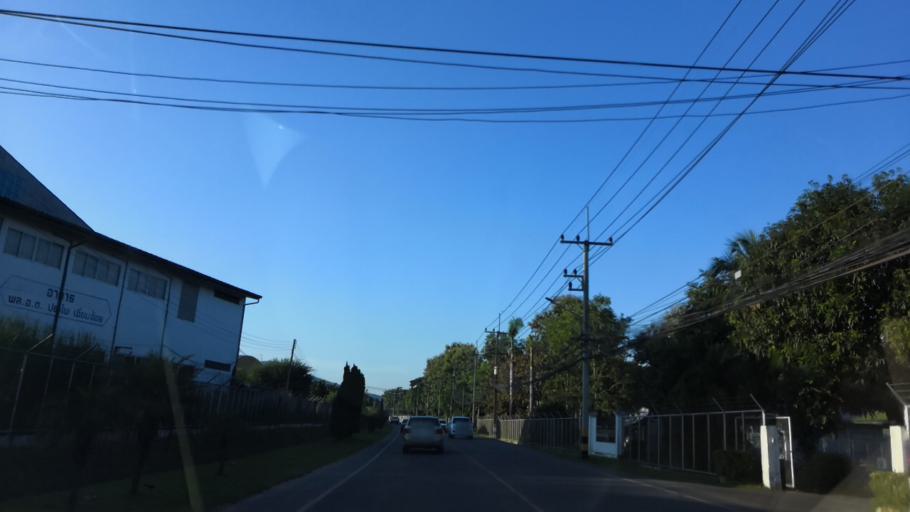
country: TH
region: Chiang Mai
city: Chiang Mai
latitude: 18.7799
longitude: 98.9667
